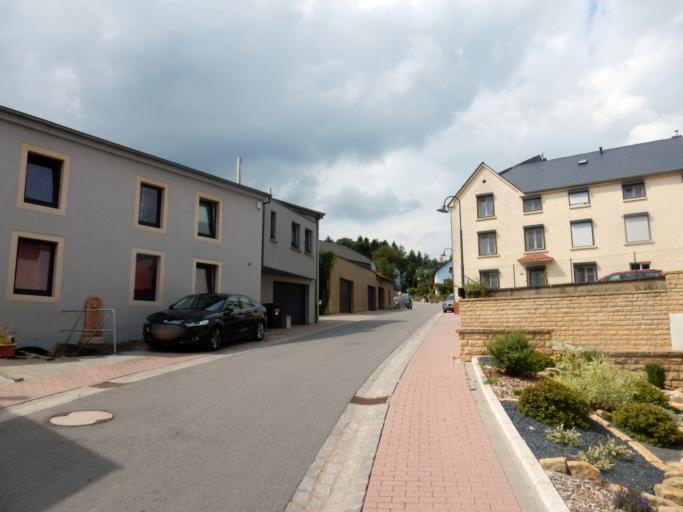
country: LU
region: Grevenmacher
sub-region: Canton de Remich
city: Stadtbredimus
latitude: 49.5639
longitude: 6.3628
